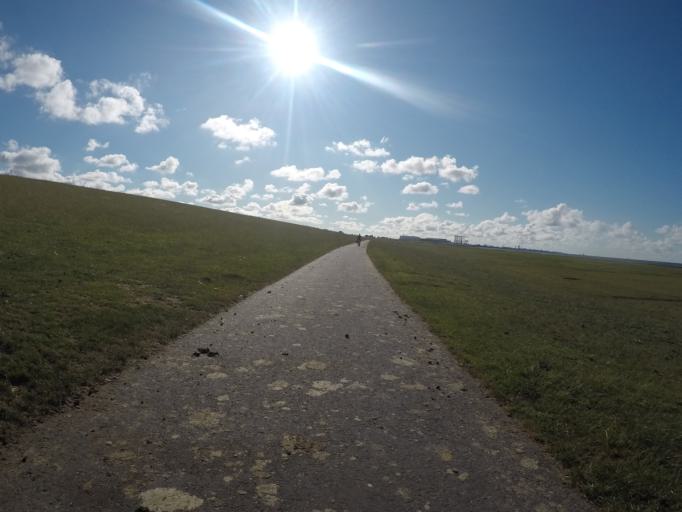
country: DE
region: Lower Saxony
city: Nordleda
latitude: 53.8325
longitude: 8.7926
